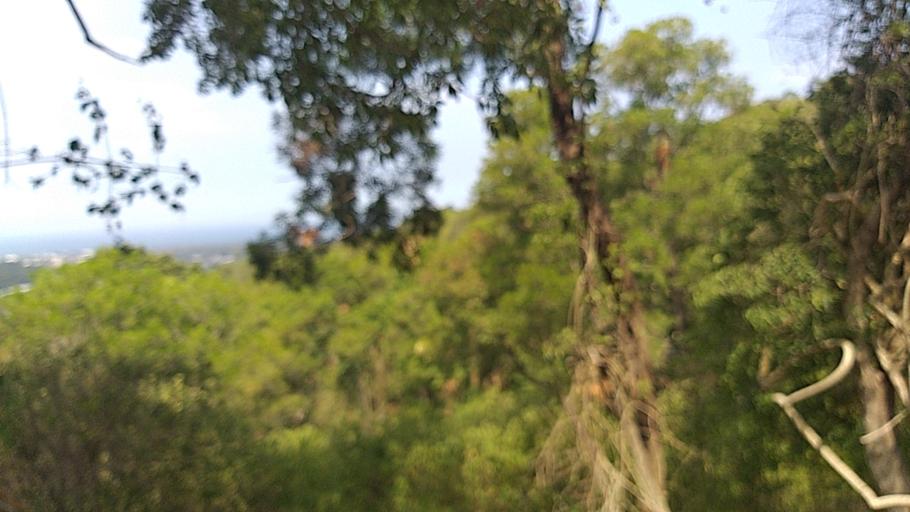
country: AU
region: New South Wales
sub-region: Wollongong
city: Mount Ousley
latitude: -34.4051
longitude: 150.8673
